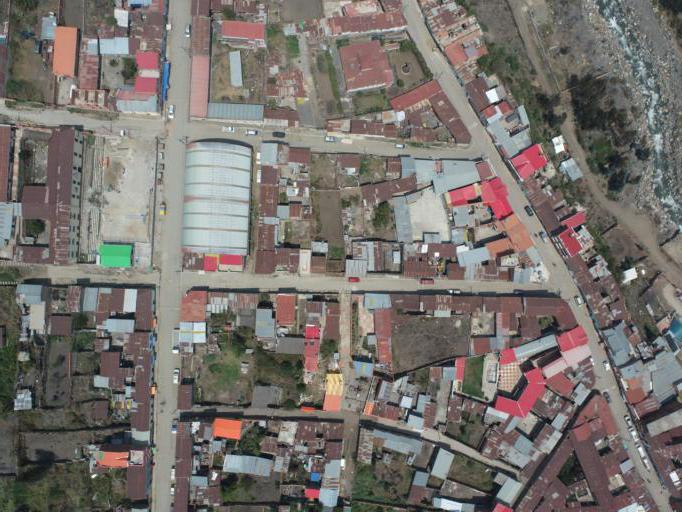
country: BO
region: La Paz
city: Quime
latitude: -16.9808
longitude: -67.2175
